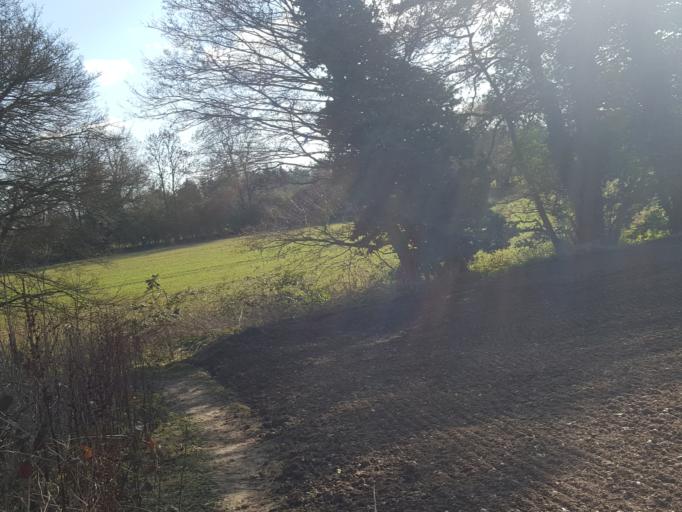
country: GB
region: England
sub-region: Essex
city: Little Clacton
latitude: 51.8633
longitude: 1.1136
